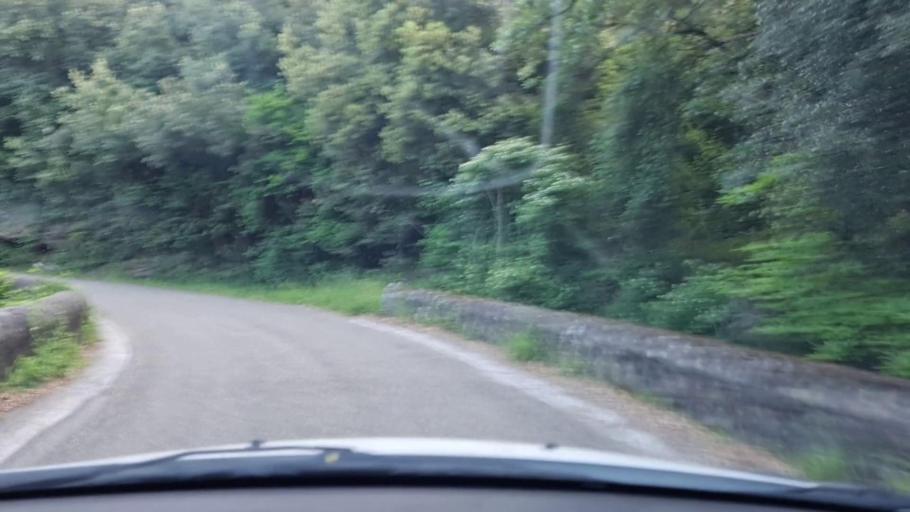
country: FR
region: Languedoc-Roussillon
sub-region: Departement du Gard
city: Les Salles-du-Gardon
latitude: 44.1721
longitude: 4.0244
